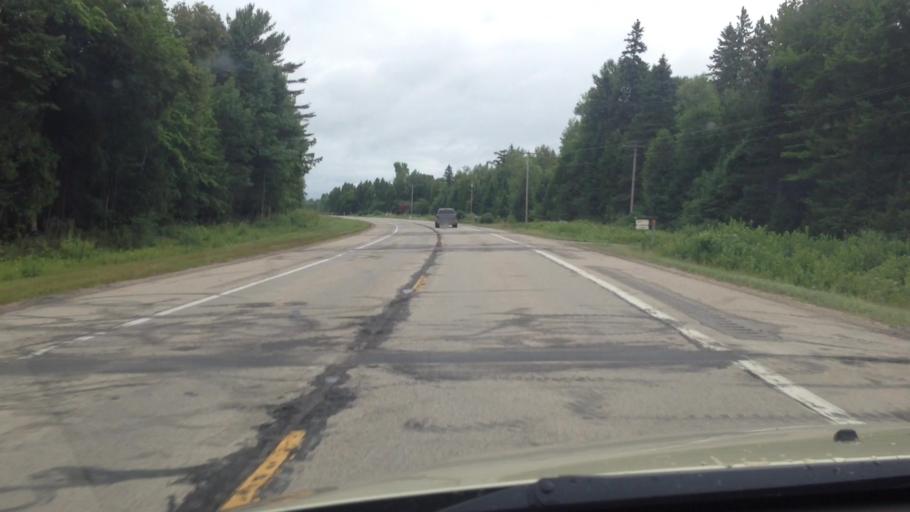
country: US
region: Michigan
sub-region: Delta County
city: Escanaba
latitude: 45.6531
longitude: -87.1790
